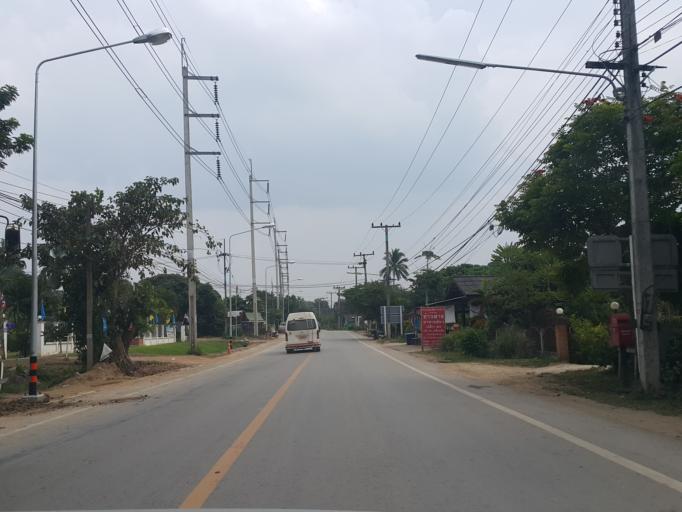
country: TH
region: Chiang Mai
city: Mae Taeng
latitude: 19.0964
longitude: 98.8476
